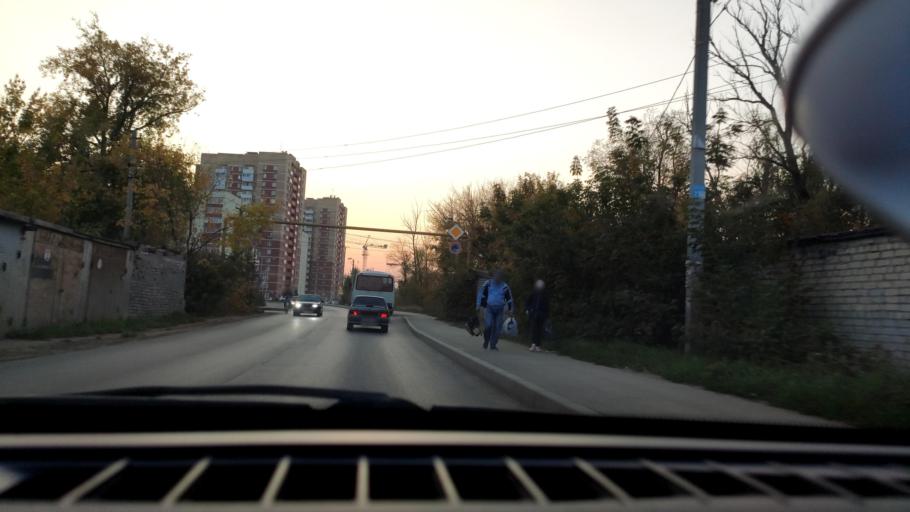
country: RU
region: Samara
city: Samara
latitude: 53.1577
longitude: 50.0824
